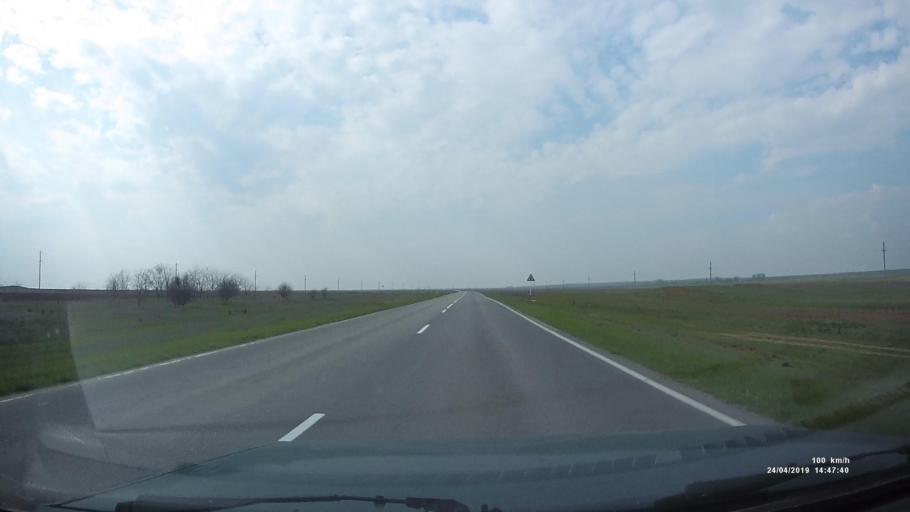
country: RU
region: Rostov
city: Remontnoye
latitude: 46.4936
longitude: 43.7692
